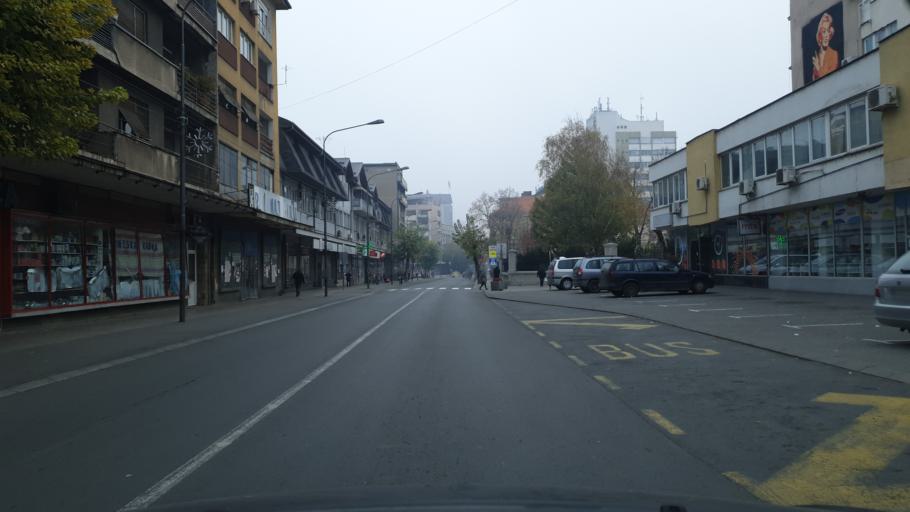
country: RS
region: Central Serbia
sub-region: Zajecarski Okrug
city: Zajecar
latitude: 43.9029
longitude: 22.2738
